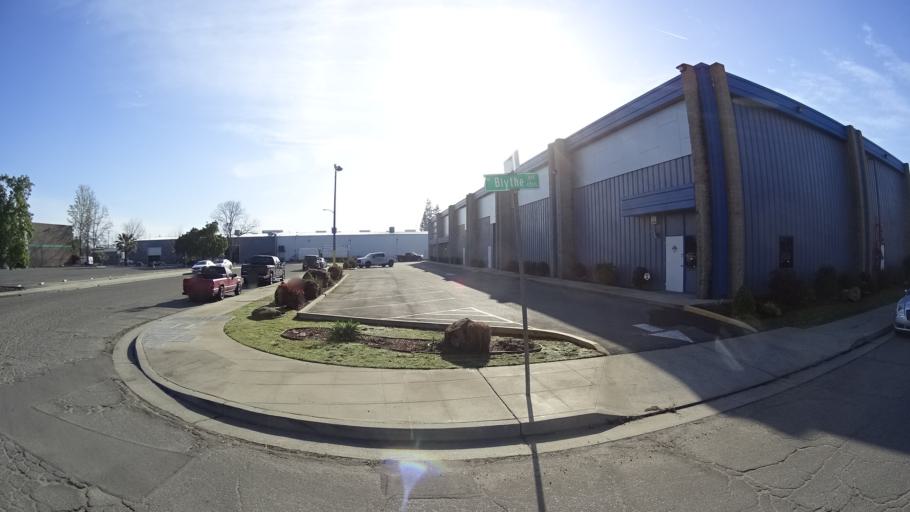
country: US
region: California
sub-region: Fresno County
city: West Park
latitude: 36.8072
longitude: -119.8726
